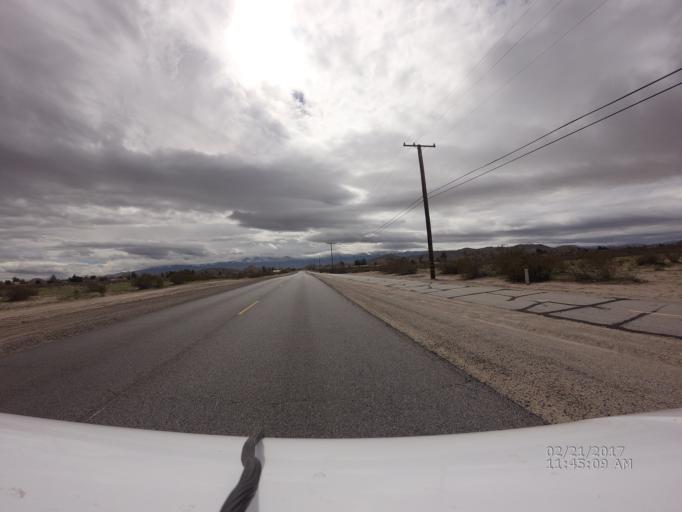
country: US
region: California
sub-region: Los Angeles County
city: Lake Los Angeles
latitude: 34.6343
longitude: -117.8269
